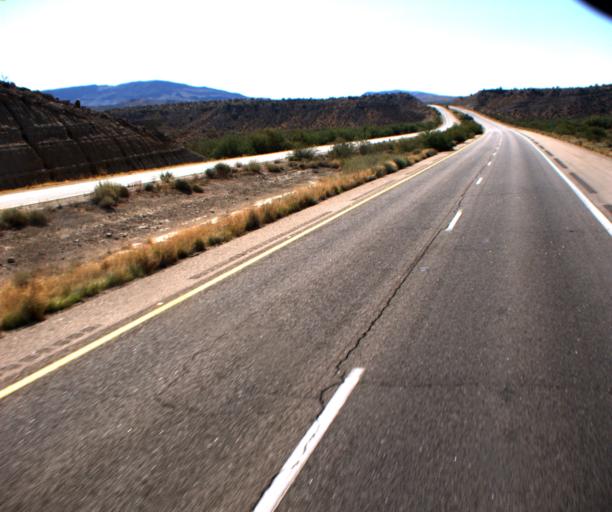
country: US
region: Arizona
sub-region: Yavapai County
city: Bagdad
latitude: 34.6410
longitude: -113.5633
